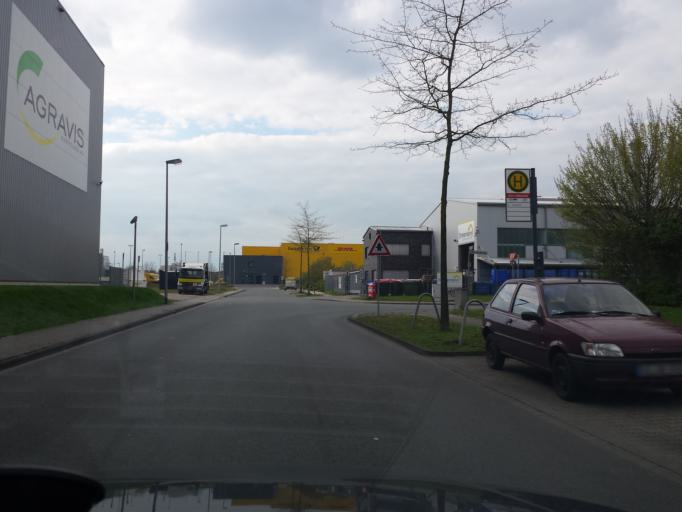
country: DE
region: North Rhine-Westphalia
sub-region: Regierungsbezirk Munster
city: Muenster
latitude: 51.9341
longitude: 7.6460
